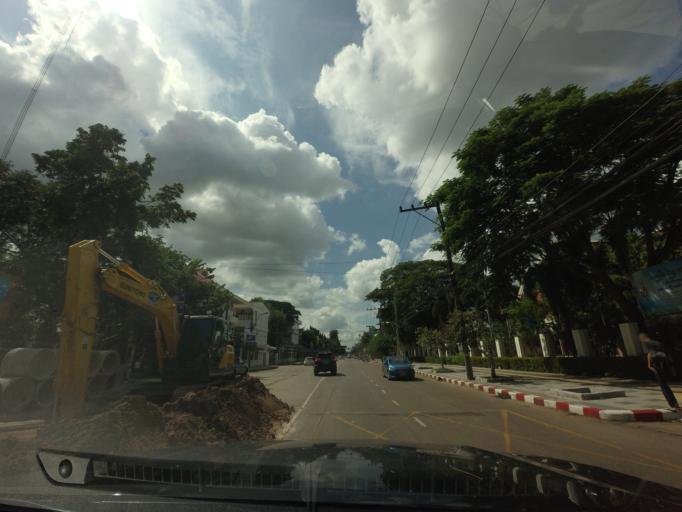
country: TH
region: Changwat Udon Thani
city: Udon Thani
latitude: 17.4064
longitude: 102.7842
